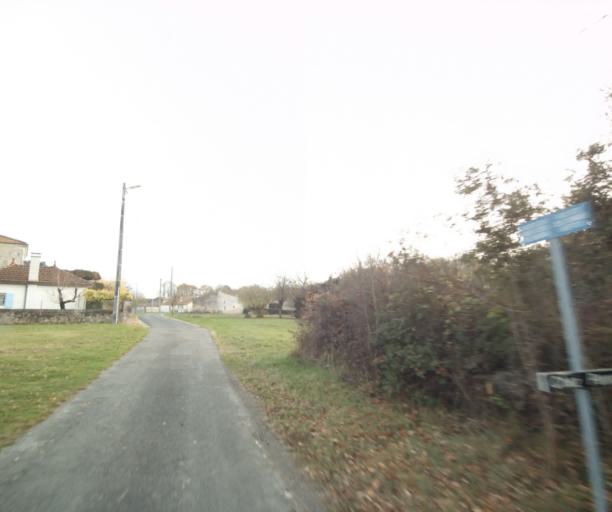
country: FR
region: Poitou-Charentes
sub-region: Departement de la Charente-Maritime
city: Saint-Hilaire-de-Villefranche
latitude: 45.8165
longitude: -0.5631
